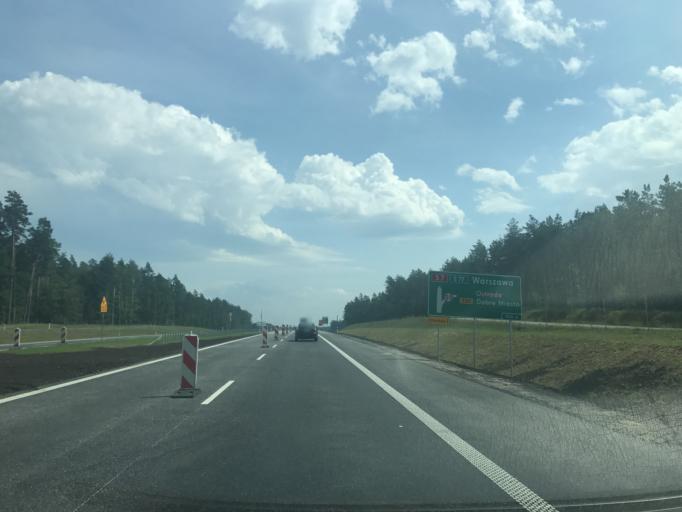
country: PL
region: Warmian-Masurian Voivodeship
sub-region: Powiat ostrodzki
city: Ostroda
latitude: 53.7330
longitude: 19.9241
